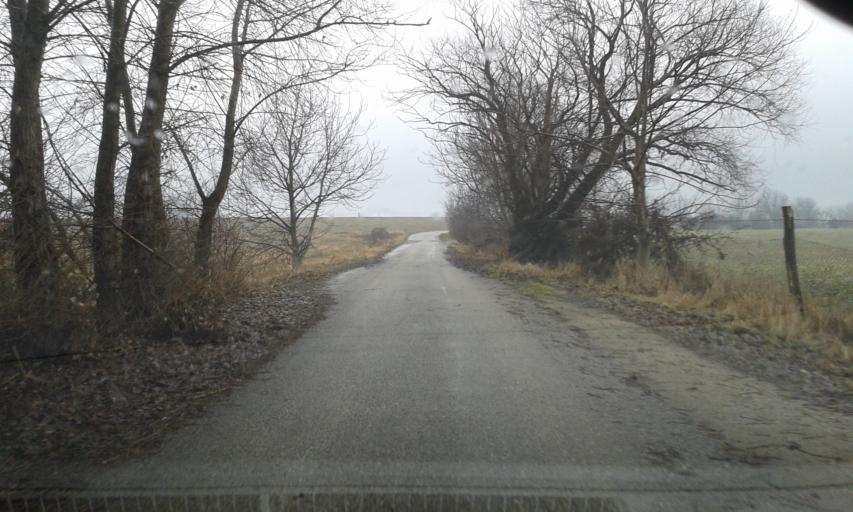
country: SK
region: Nitriansky
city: Tlmace
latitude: 48.2773
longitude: 18.5213
